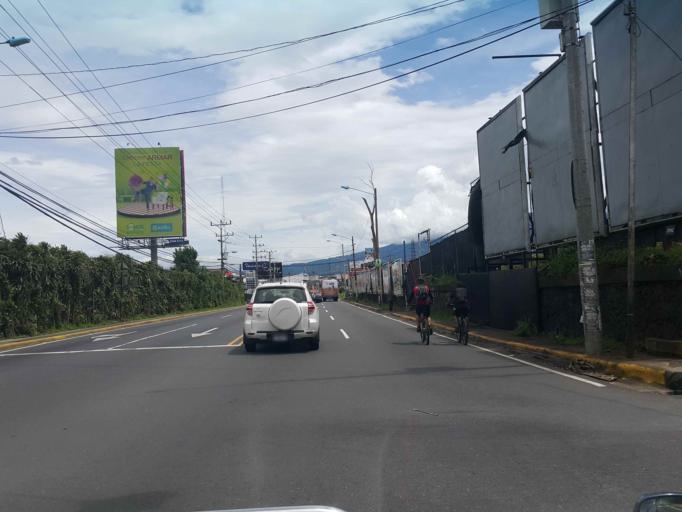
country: CR
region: Heredia
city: San Pablo
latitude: 9.9864
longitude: -84.1102
